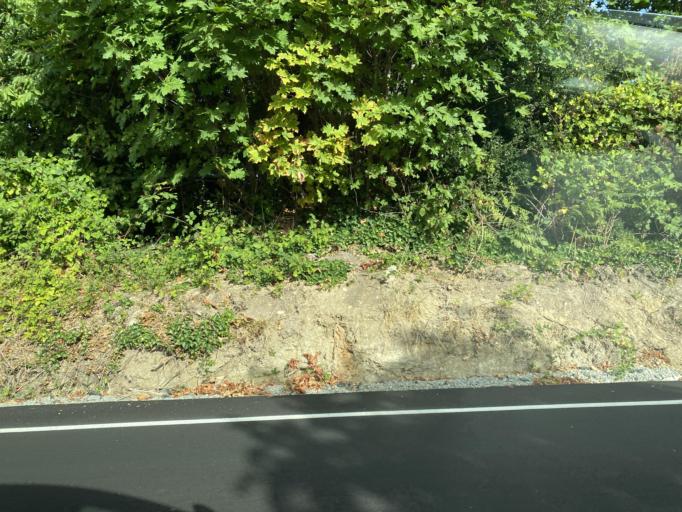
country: US
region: Washington
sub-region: Island County
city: Freeland
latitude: 48.0128
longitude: -122.5367
